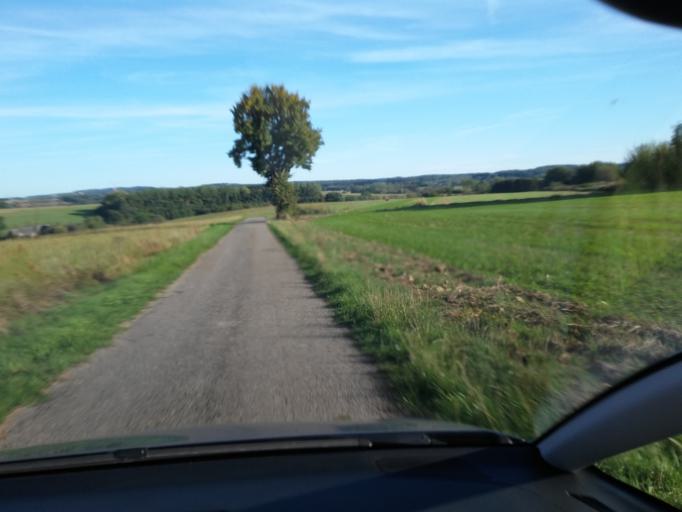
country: BE
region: Wallonia
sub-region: Province du Luxembourg
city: Habay-la-Vieille
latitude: 49.7092
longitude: 5.7000
